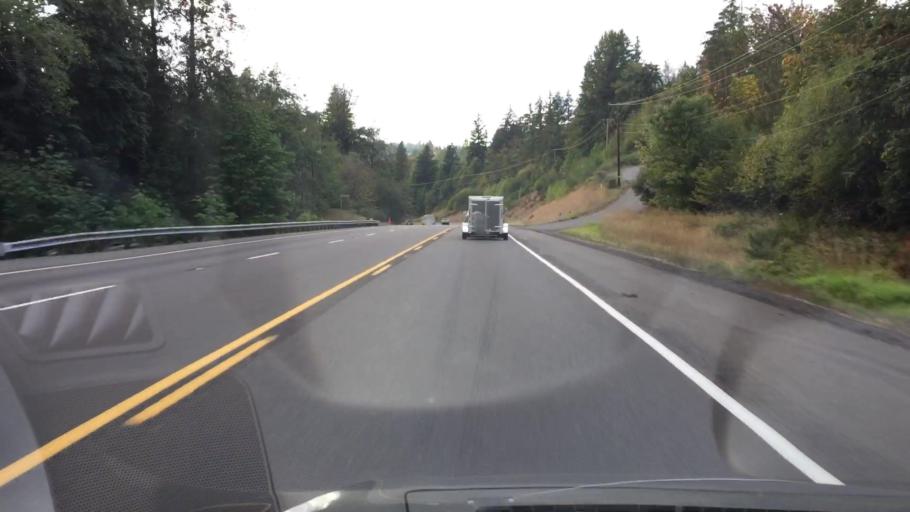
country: US
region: Washington
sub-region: Lewis County
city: Napavine
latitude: 46.5315
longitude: -122.6096
